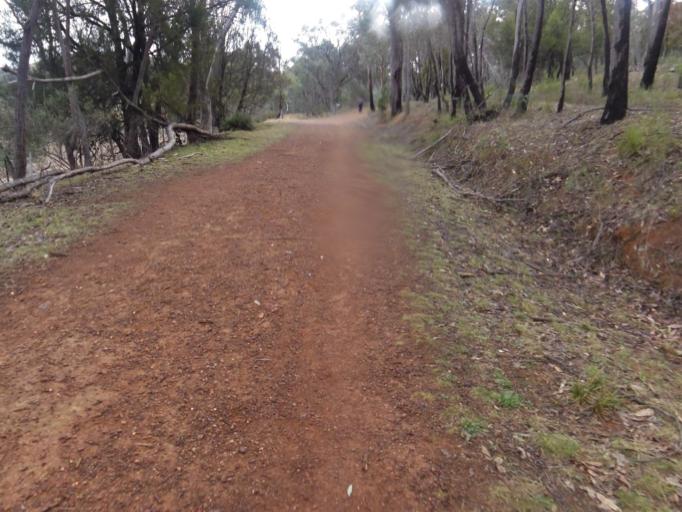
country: AU
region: Australian Capital Territory
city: Macquarie
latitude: -35.2726
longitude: 149.0794
